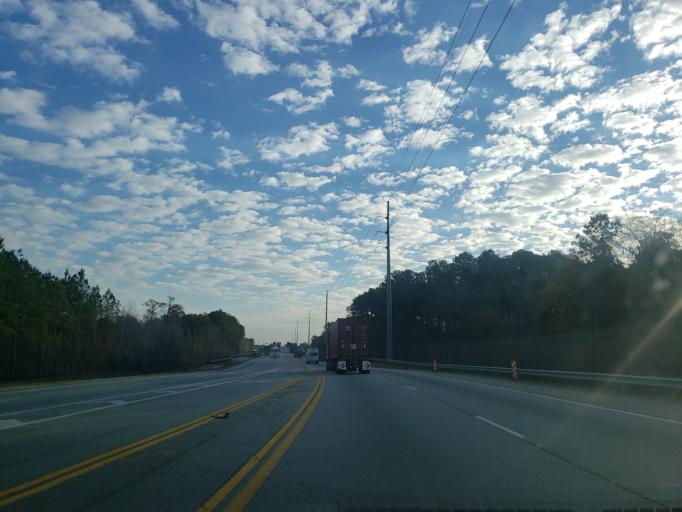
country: US
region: Georgia
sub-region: Chatham County
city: Port Wentworth
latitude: 32.1630
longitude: -81.2091
